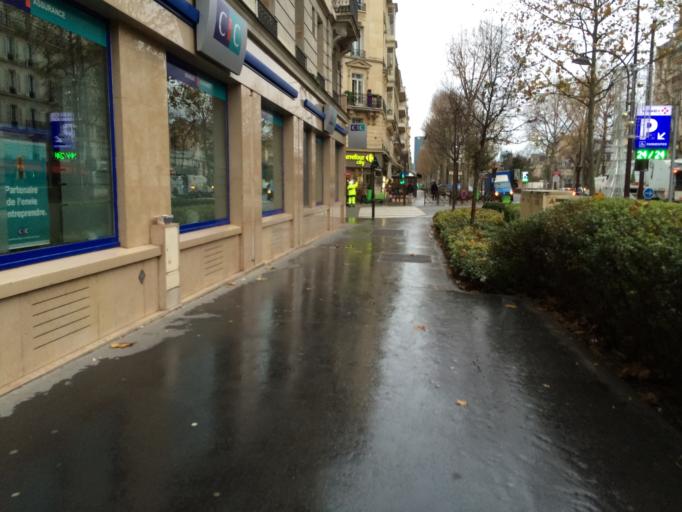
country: FR
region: Ile-de-France
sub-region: Departement des Hauts-de-Seine
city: Neuilly-sur-Seine
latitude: 48.8825
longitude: 2.2779
